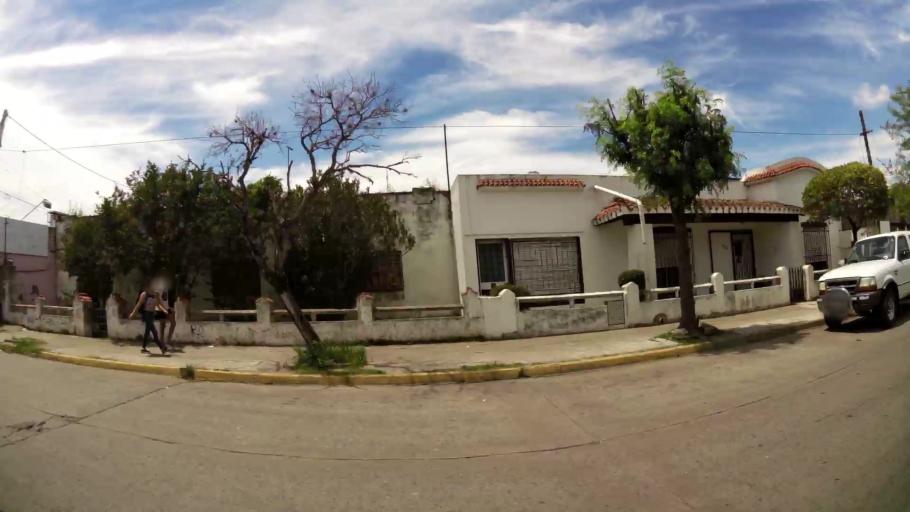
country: AR
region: Santa Fe
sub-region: Departamento de Rosario
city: Rosario
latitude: -32.9886
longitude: -60.6284
